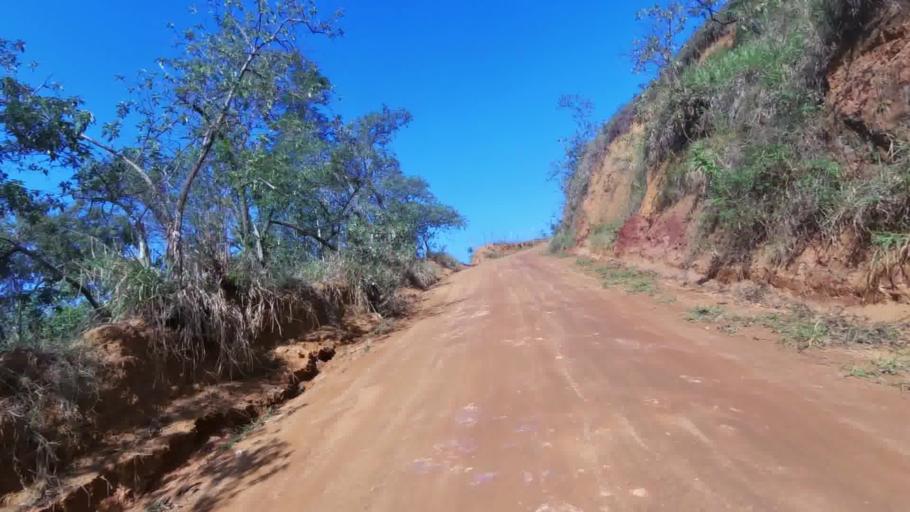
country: BR
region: Espirito Santo
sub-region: Alfredo Chaves
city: Alfredo Chaves
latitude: -20.6831
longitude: -40.7795
